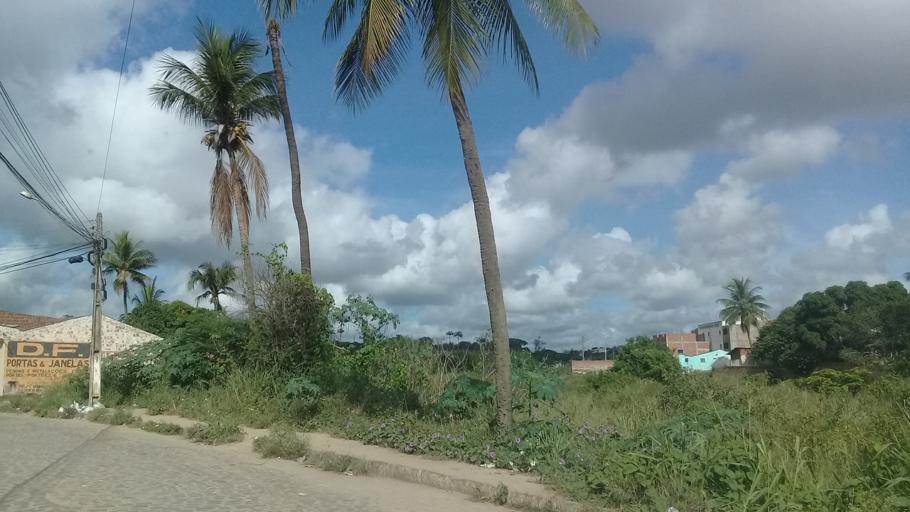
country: BR
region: Pernambuco
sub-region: Vitoria De Santo Antao
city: Vitoria de Santo Antao
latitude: -8.1258
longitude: -35.2960
